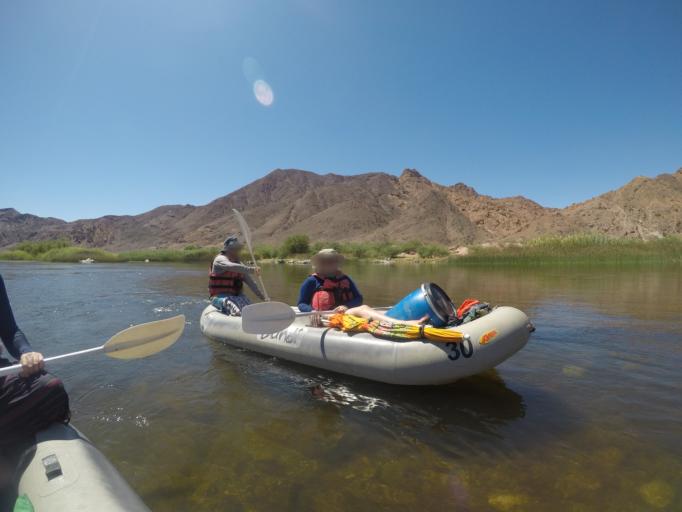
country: ZA
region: Northern Cape
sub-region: Namakwa District Municipality
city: Port Nolloth
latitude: -28.7243
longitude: 17.4233
